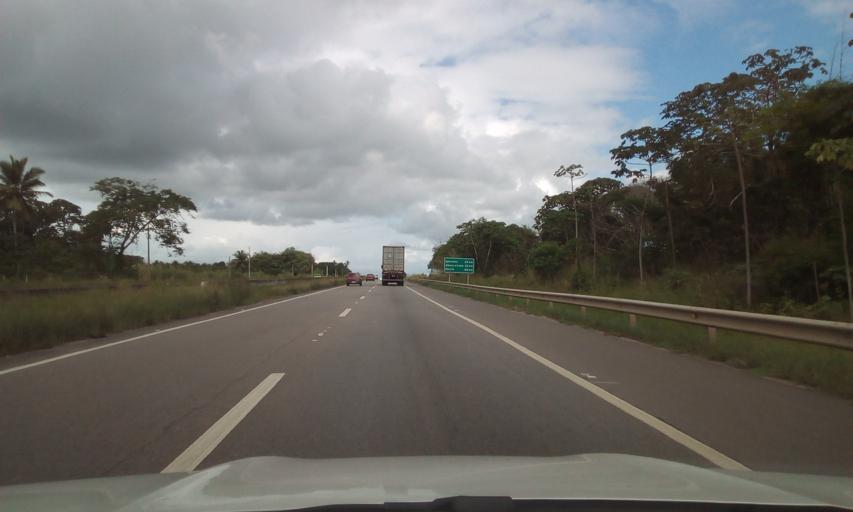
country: BR
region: Pernambuco
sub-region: Goiana
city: Goiana
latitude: -7.6409
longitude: -34.9559
